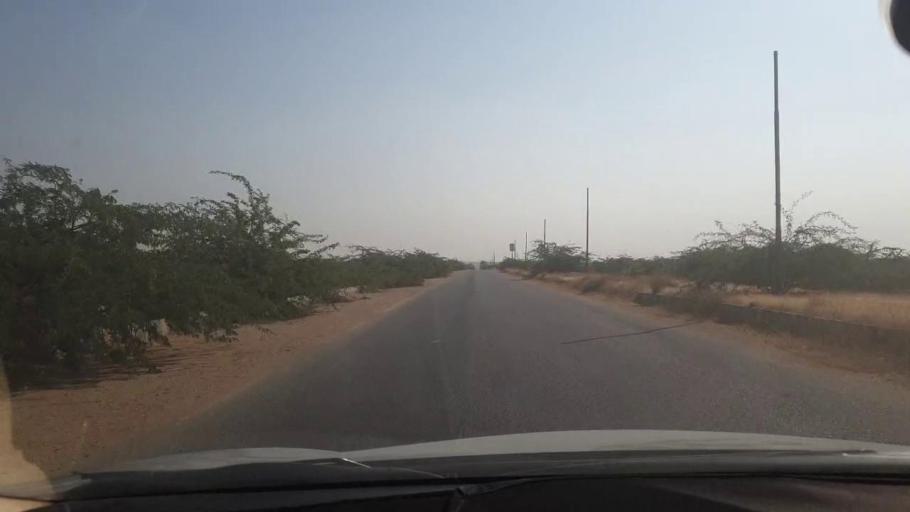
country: PK
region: Sindh
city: Malir Cantonment
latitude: 25.0636
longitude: 67.1391
